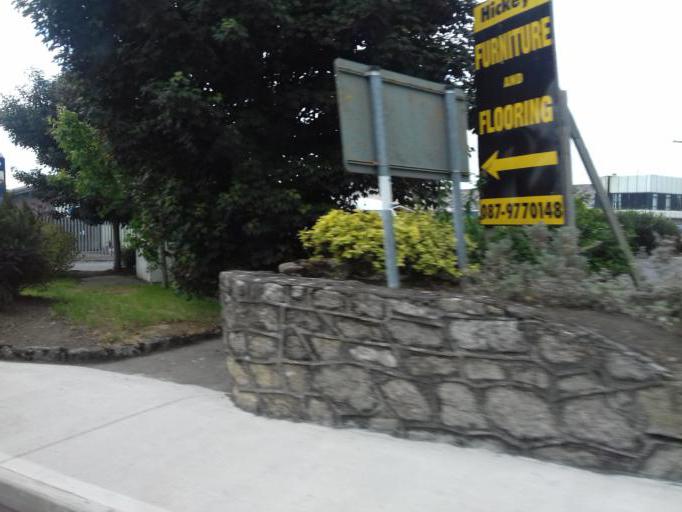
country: IE
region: Leinster
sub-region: County Carlow
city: Tullow
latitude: 52.7955
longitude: -6.7481
